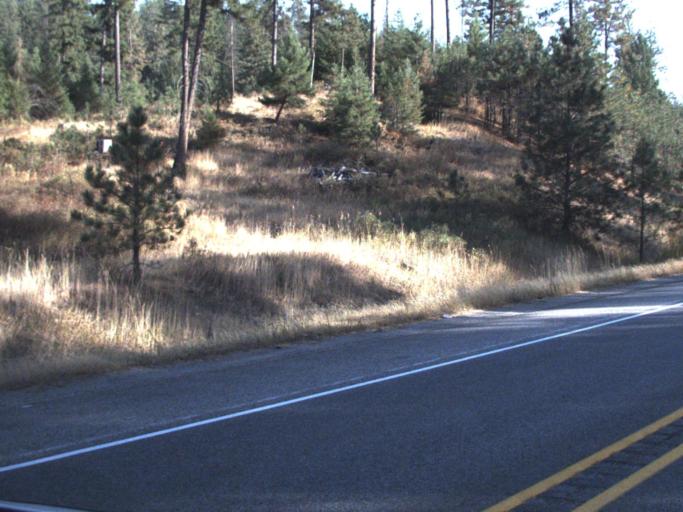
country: US
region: Washington
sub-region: Spokane County
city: Deer Park
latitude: 47.9287
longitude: -117.3515
